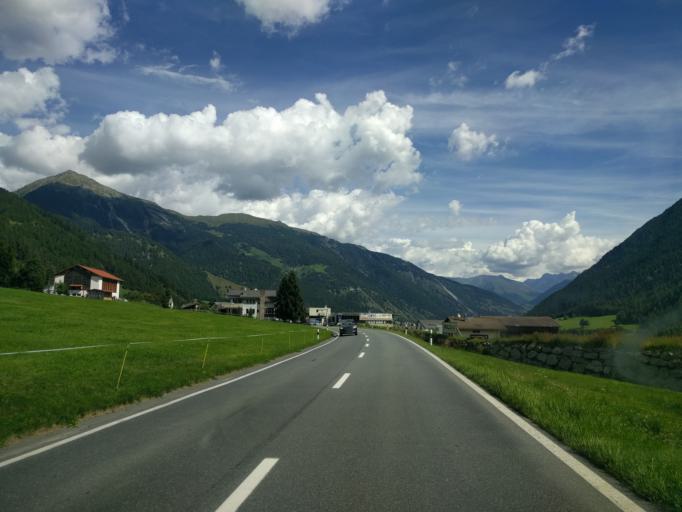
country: IT
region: Trentino-Alto Adige
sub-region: Bolzano
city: Tubre
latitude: 46.6184
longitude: 10.4450
